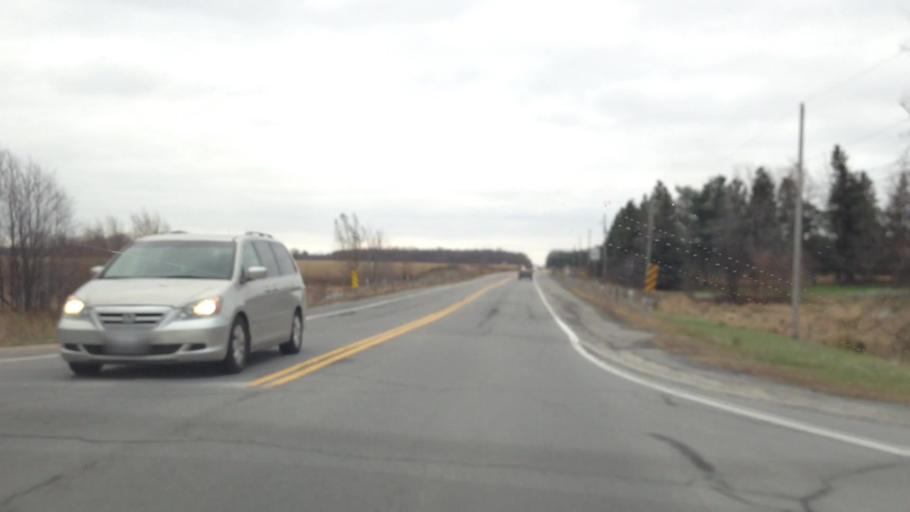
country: CA
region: Ontario
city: Clarence-Rockland
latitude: 45.3717
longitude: -75.3795
